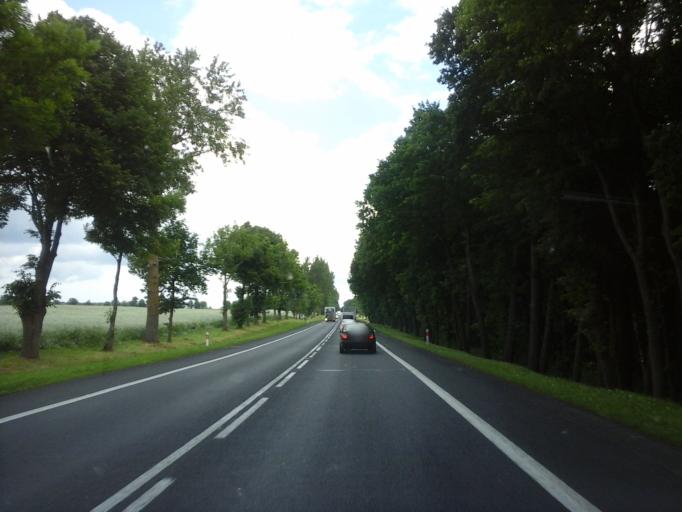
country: PL
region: West Pomeranian Voivodeship
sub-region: Powiat bialogardzki
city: Bialogard
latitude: 54.0915
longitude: 15.9908
